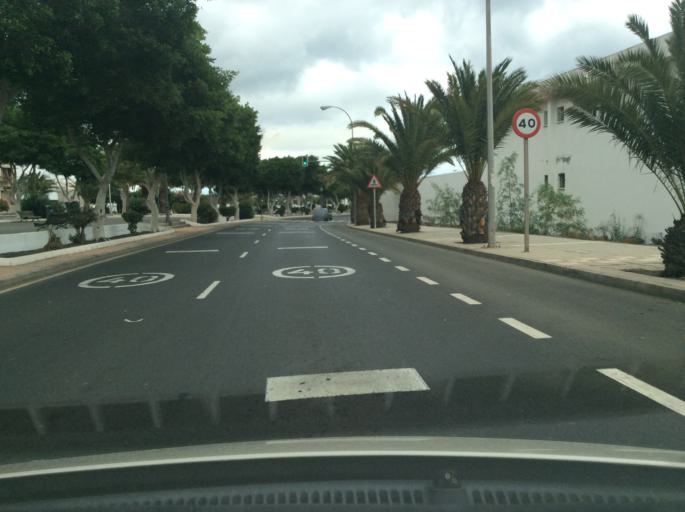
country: ES
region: Canary Islands
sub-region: Provincia de Las Palmas
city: Arrecife
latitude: 28.9669
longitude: -13.5499
